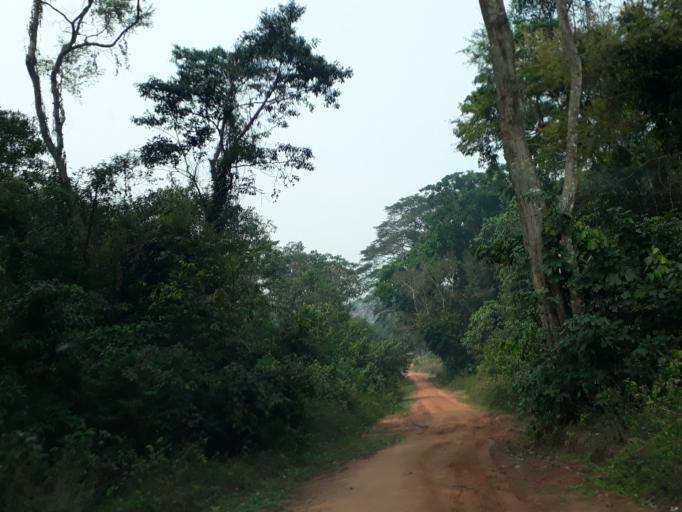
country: CD
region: Kasai-Occidental
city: Tshikapa
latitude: -6.1619
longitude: 20.4224
